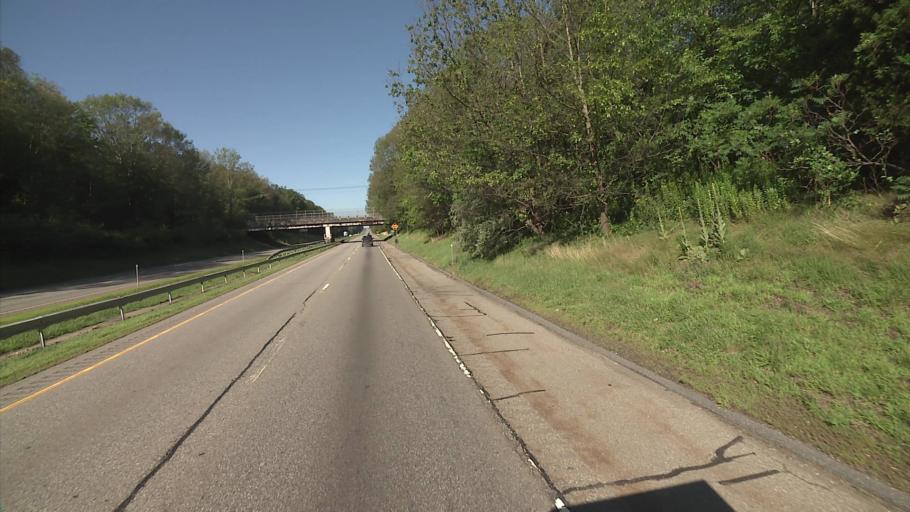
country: US
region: Connecticut
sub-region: New London County
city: Baltic
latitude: 41.5818
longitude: -72.0681
